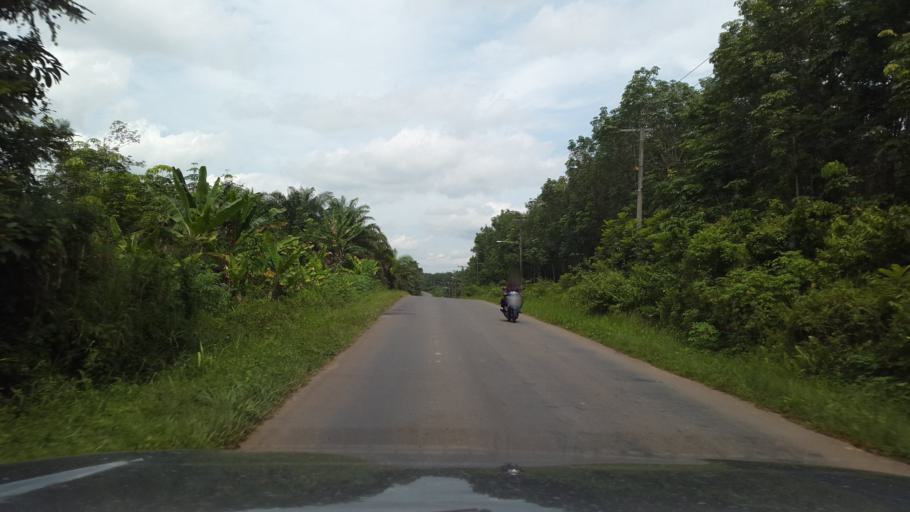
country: ID
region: South Sumatra
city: Gunungmegang Dalam
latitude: -3.3715
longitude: 103.9439
